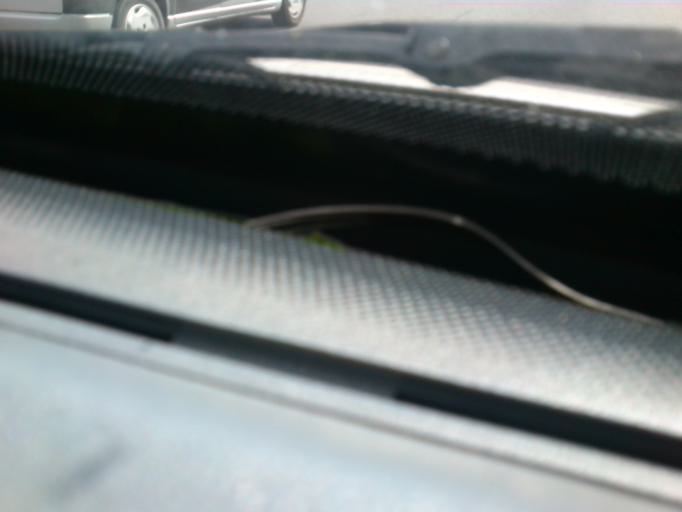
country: CZ
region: Praha
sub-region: Praha 8
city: Karlin
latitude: 50.0907
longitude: 14.4376
